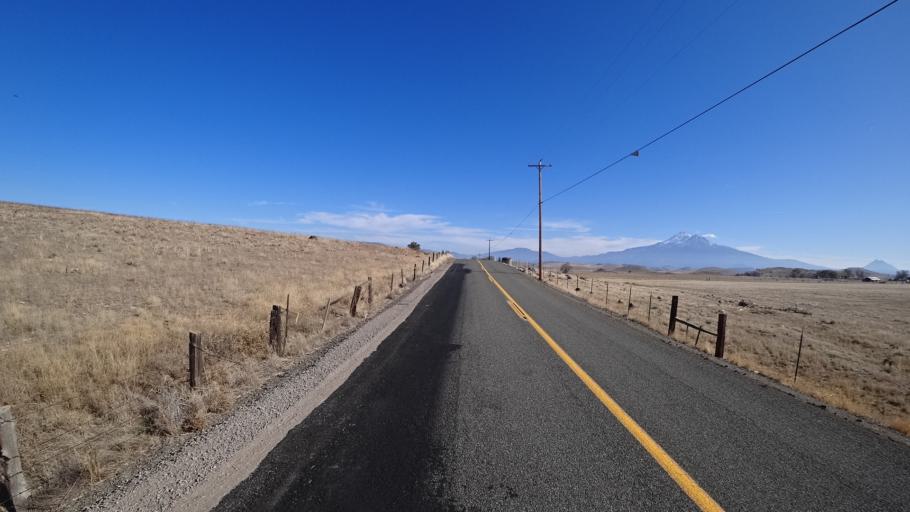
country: US
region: California
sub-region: Siskiyou County
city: Montague
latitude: 41.5747
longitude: -122.5335
